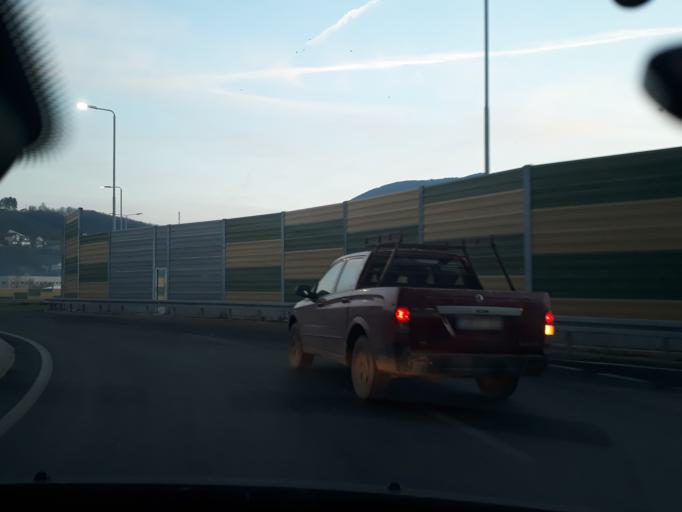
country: BA
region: Federation of Bosnia and Herzegovina
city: Hadzici
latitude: 43.8612
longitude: 18.2493
